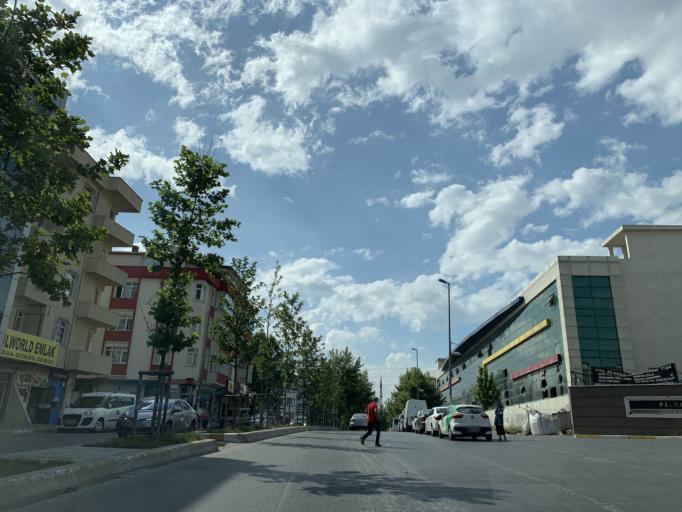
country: TR
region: Istanbul
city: Esenyurt
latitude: 41.0382
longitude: 28.6639
